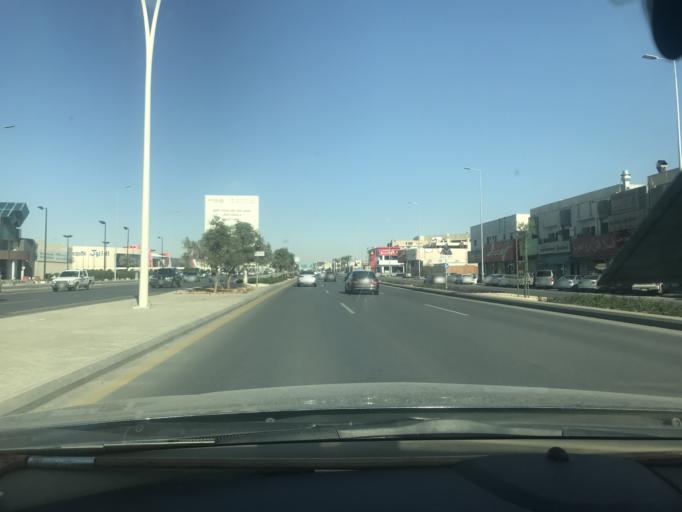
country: SA
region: Ar Riyad
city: Riyadh
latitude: 24.7397
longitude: 46.6837
